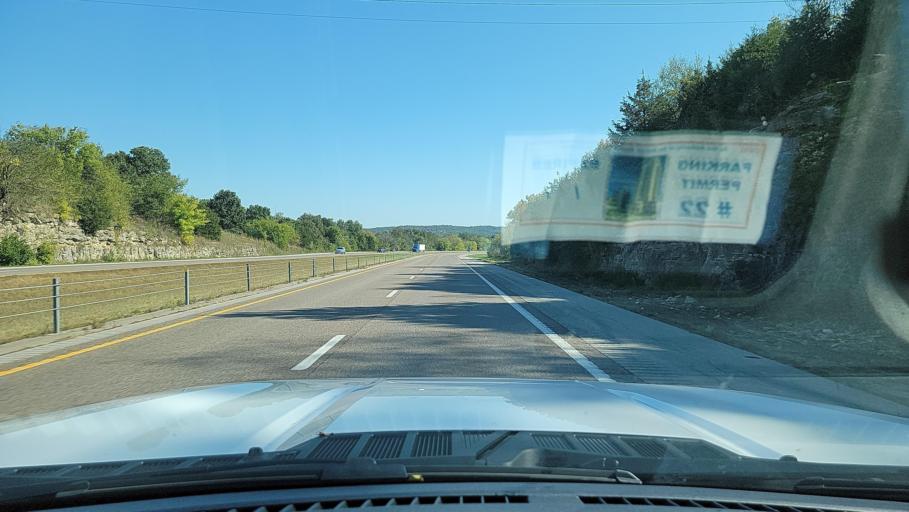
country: US
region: Missouri
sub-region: Jefferson County
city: Crystal City
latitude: 38.1320
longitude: -90.3179
